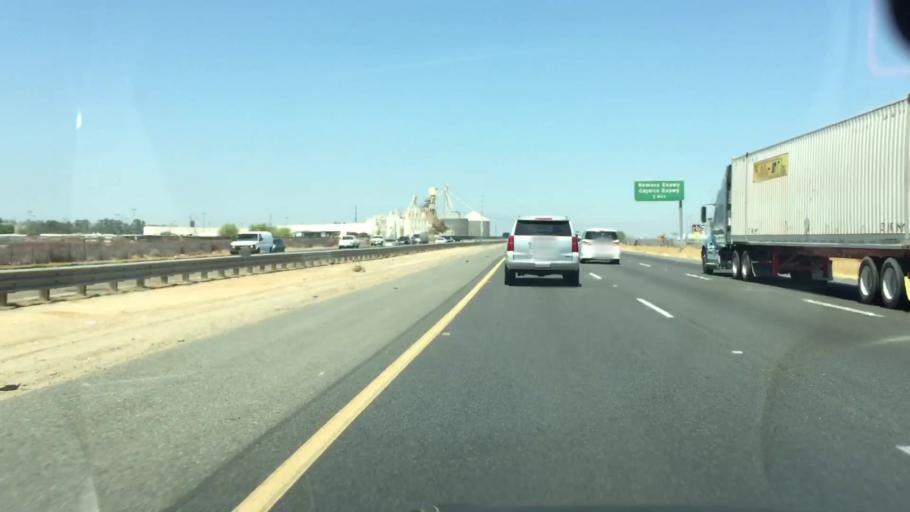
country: US
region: California
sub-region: Riverside County
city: Perris
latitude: 33.8266
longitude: -117.2433
